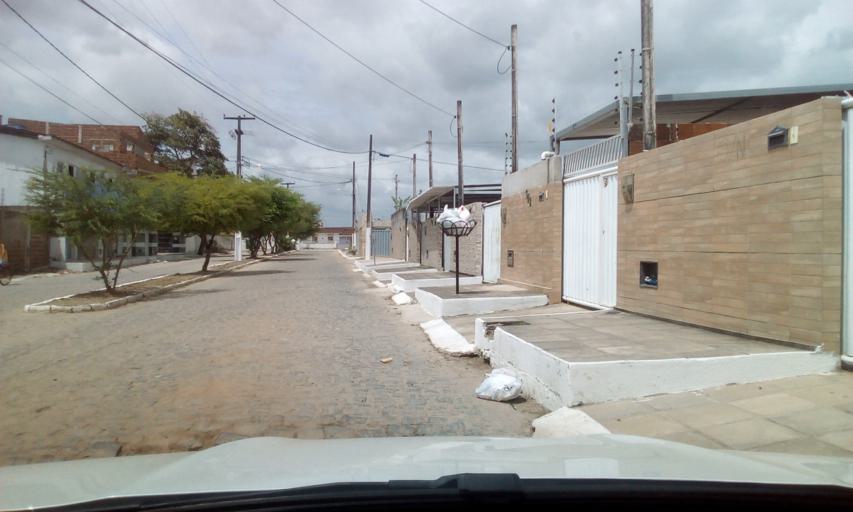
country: BR
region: Paraiba
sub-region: Bayeux
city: Bayeux
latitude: -7.1338
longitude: -34.9528
